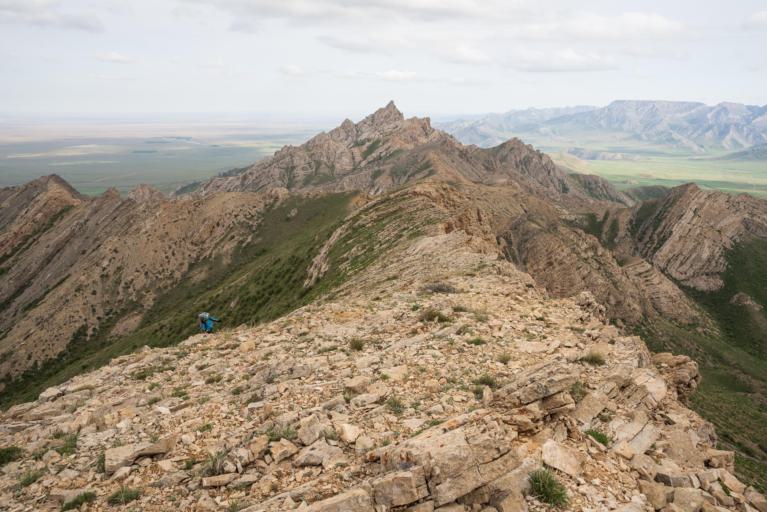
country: KZ
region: Ongtustik Qazaqstan
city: Ashchysay
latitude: 43.7549
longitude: 68.8165
